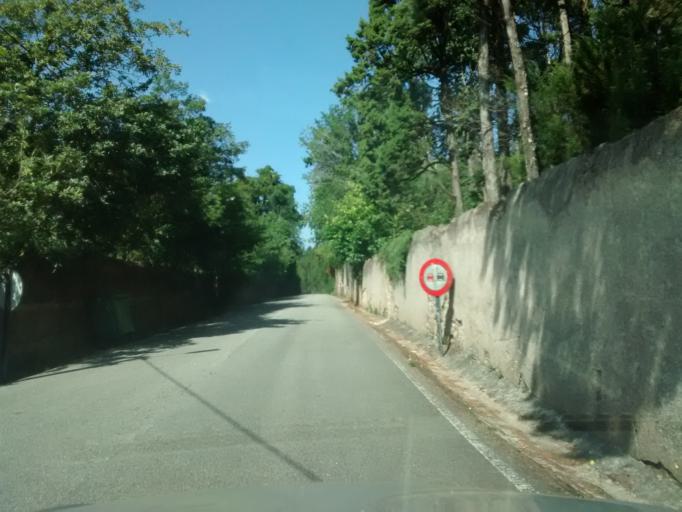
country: PT
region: Aveiro
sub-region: Mealhada
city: Pampilhosa do Botao
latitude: 40.3808
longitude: -8.3769
